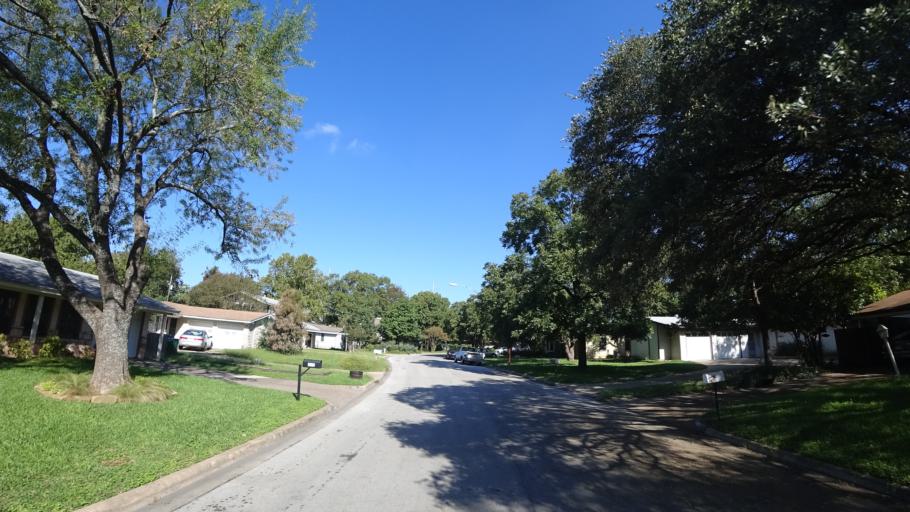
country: US
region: Texas
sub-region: Travis County
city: Austin
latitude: 30.3421
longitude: -97.7142
